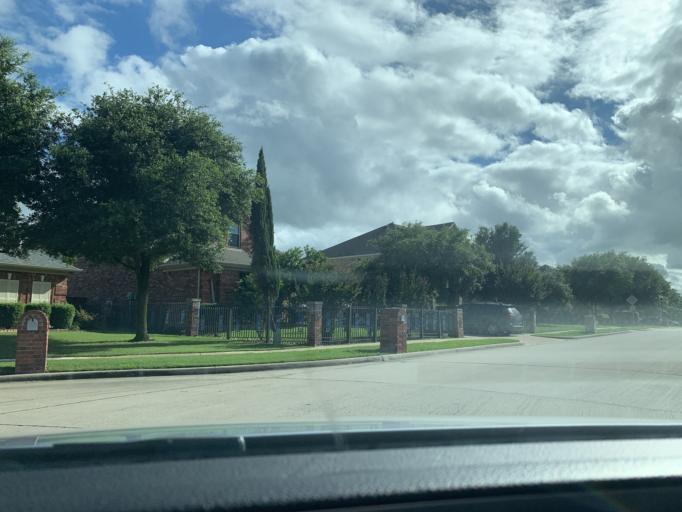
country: US
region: Texas
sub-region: Dallas County
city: Cedar Hill
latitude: 32.6401
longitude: -97.0428
